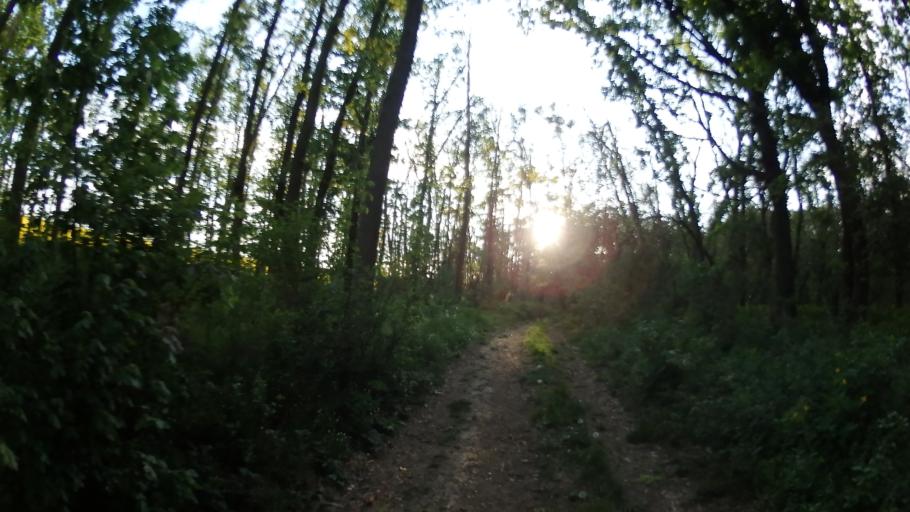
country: CZ
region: South Moravian
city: Zelesice
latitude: 49.1319
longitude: 16.5747
